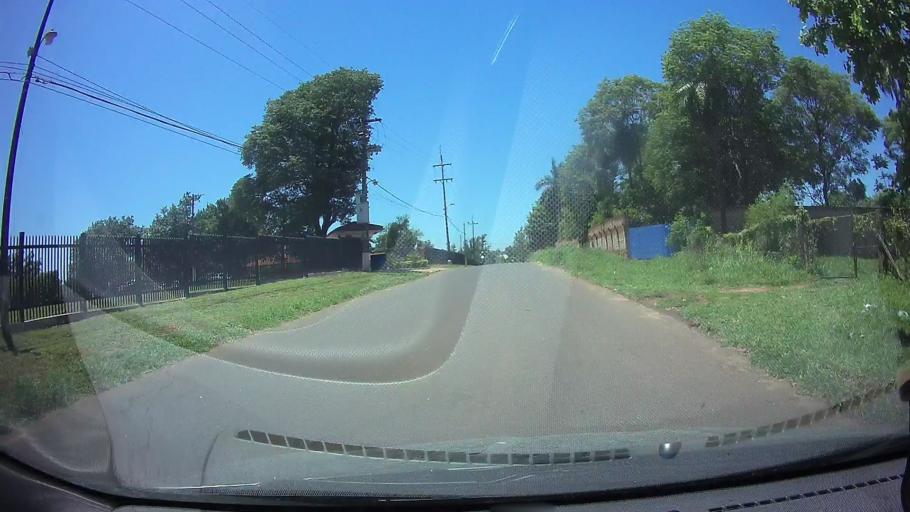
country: PY
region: Central
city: San Lorenzo
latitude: -25.3522
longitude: -57.4895
